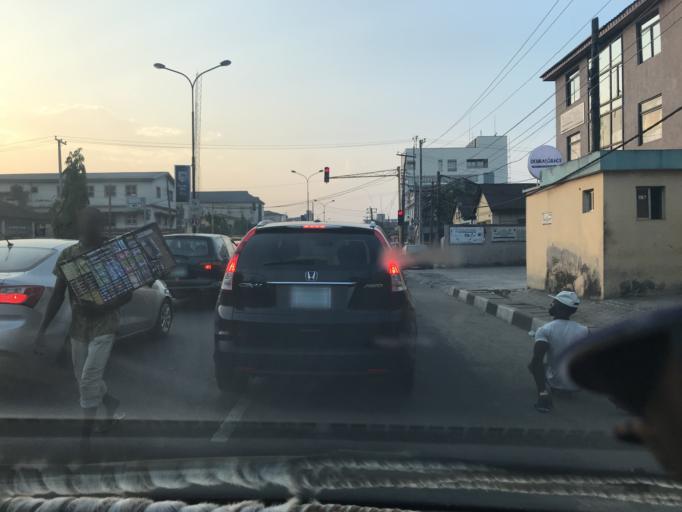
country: NG
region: Lagos
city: Makoko
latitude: 6.4953
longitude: 3.3807
